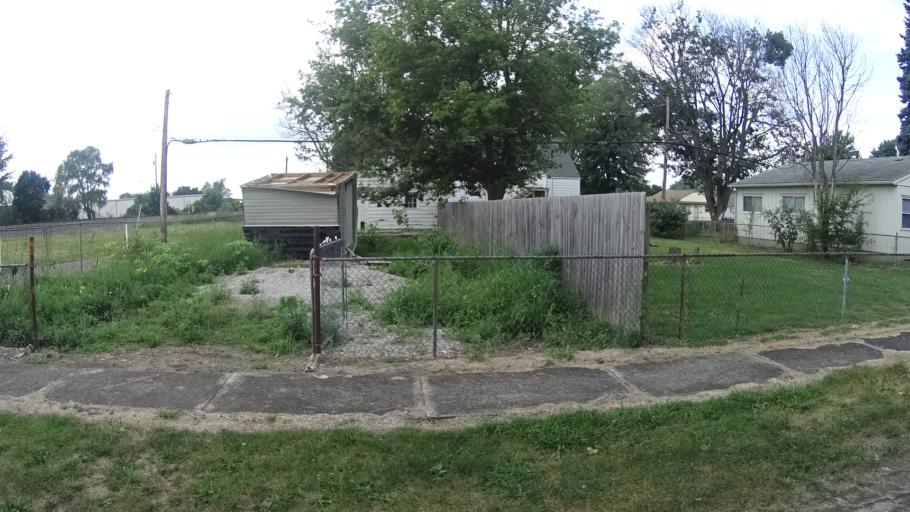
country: US
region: Ohio
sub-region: Erie County
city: Sandusky
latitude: 41.4434
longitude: -82.7456
